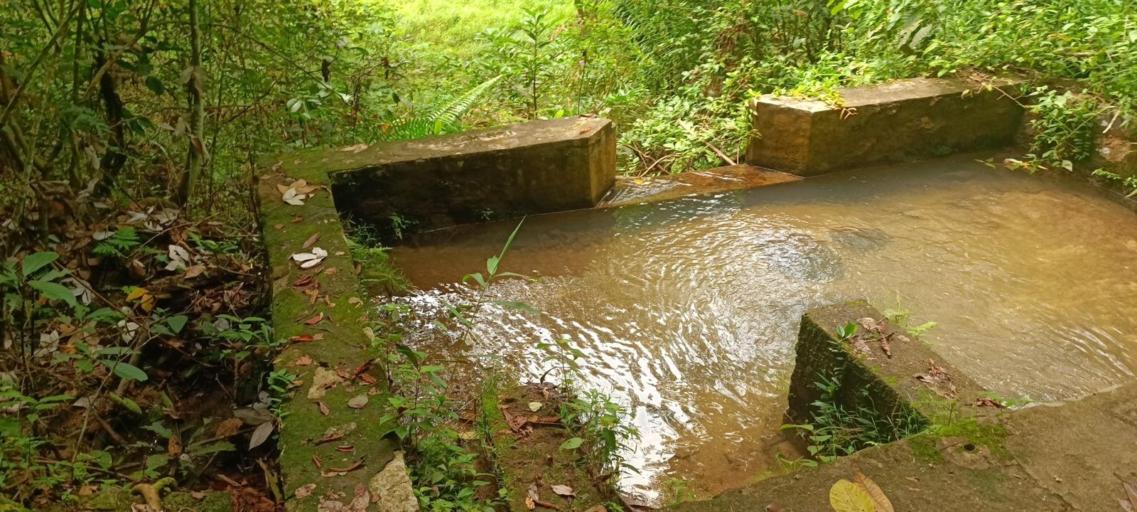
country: MY
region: Penang
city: Bukit Mertajam
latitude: 5.3725
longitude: 100.4950
